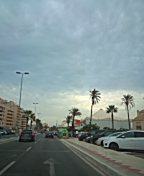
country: ES
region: Murcia
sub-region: Murcia
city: La Manga del Mar Menor
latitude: 37.7066
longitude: -0.7426
